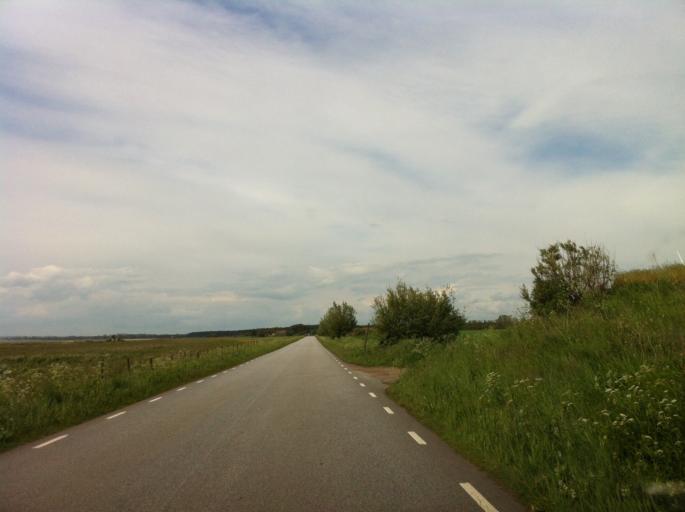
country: SE
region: Skane
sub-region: Kavlinge Kommun
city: Hofterup
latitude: 55.7788
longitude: 12.9345
